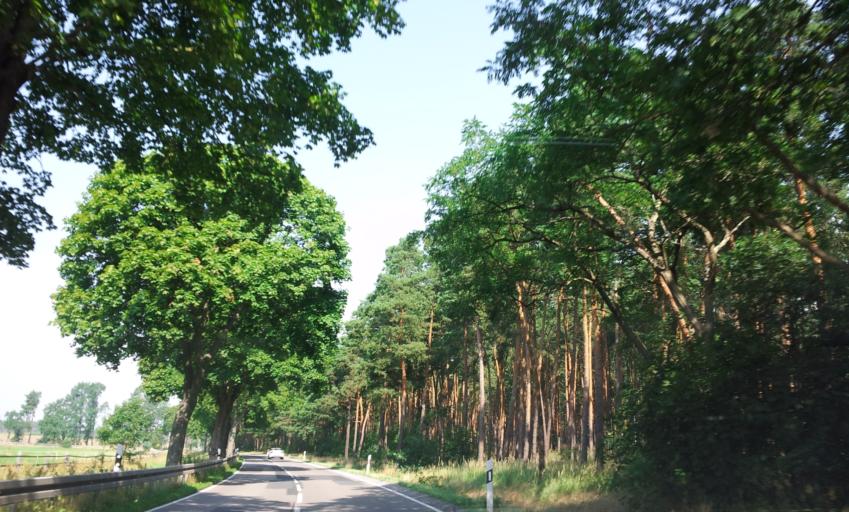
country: DE
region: Brandenburg
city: Linthe
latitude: 52.1199
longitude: 12.8153
